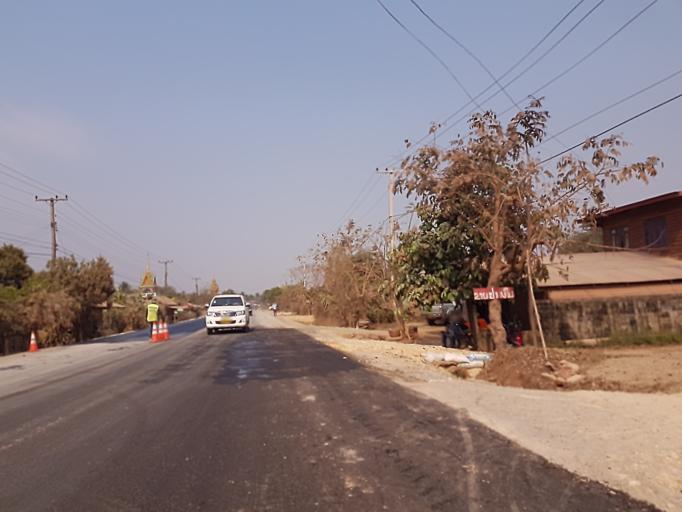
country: TH
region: Nong Khai
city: Nong Khai
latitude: 17.9330
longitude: 102.7794
